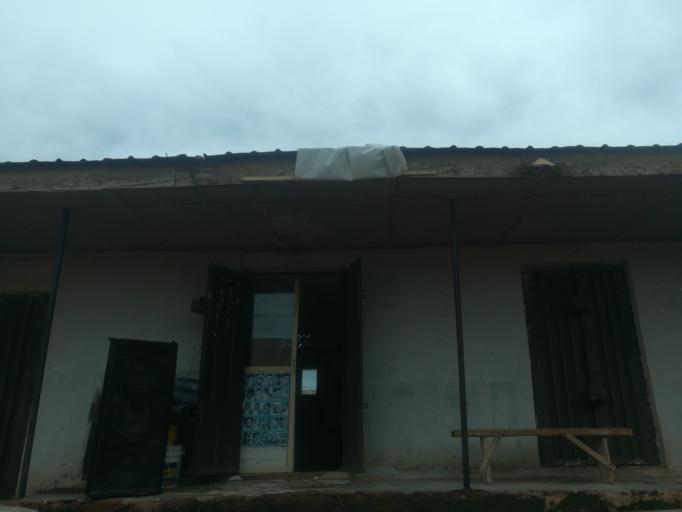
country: NG
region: Oyo
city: Ibadan
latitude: 7.3188
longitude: 3.8842
